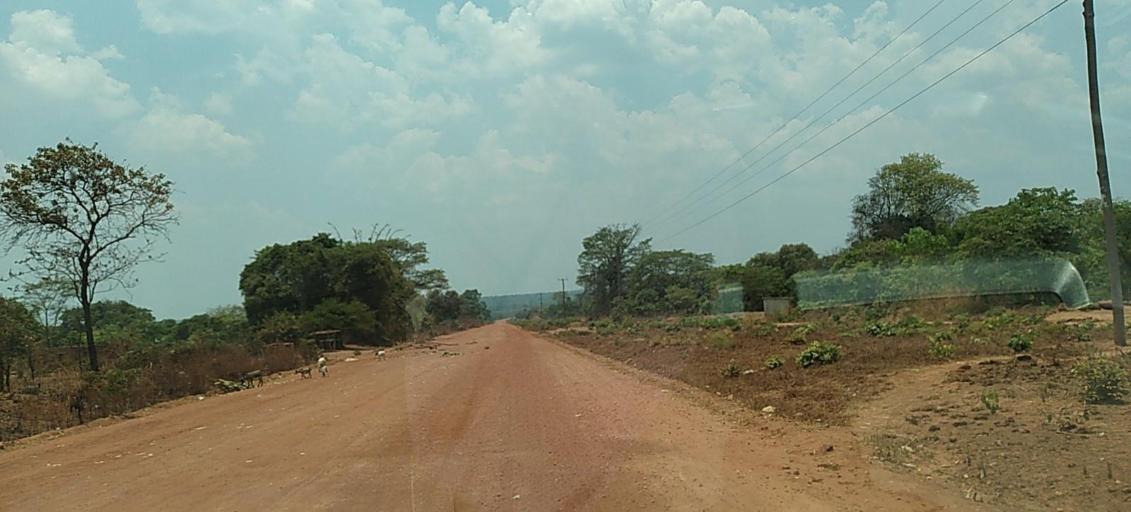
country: ZM
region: Copperbelt
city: Chingola
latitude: -12.8788
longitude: 27.5918
